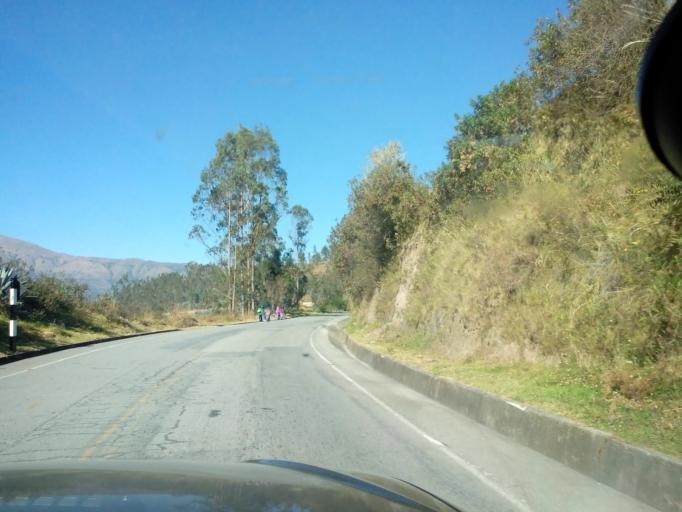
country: PE
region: Apurimac
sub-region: Provincia de Abancay
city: Tamburco
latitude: -13.6073
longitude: -72.8508
